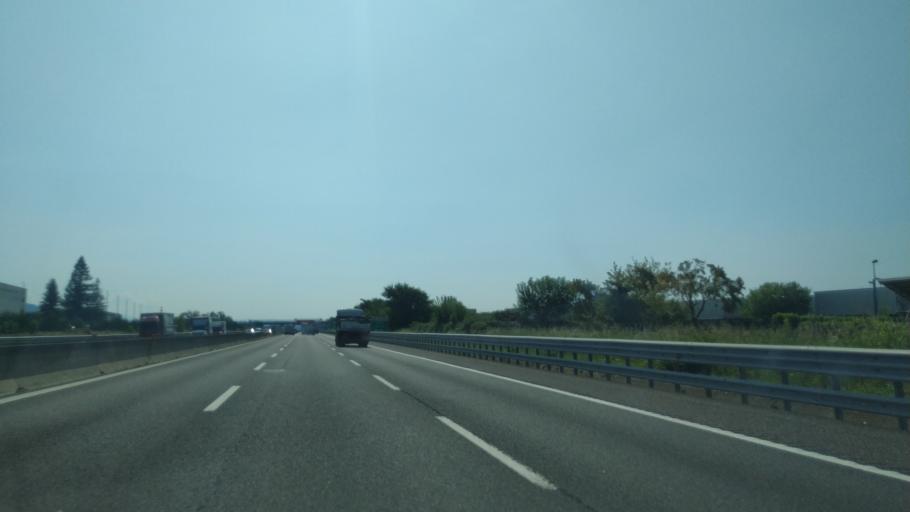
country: IT
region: Lombardy
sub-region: Provincia di Bergamo
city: Grumello del Monte
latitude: 45.6272
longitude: 9.8815
